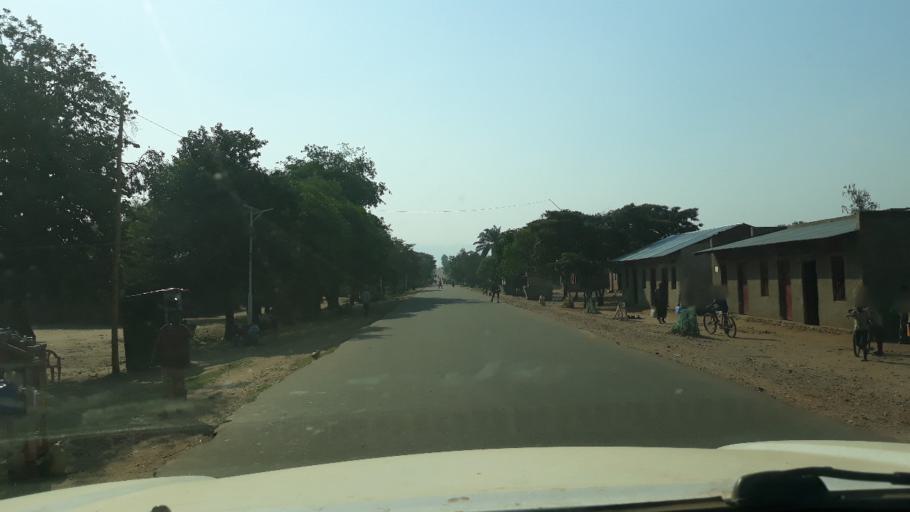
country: BI
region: Cibitoke
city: Cibitoke
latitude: -2.8531
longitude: 29.0262
